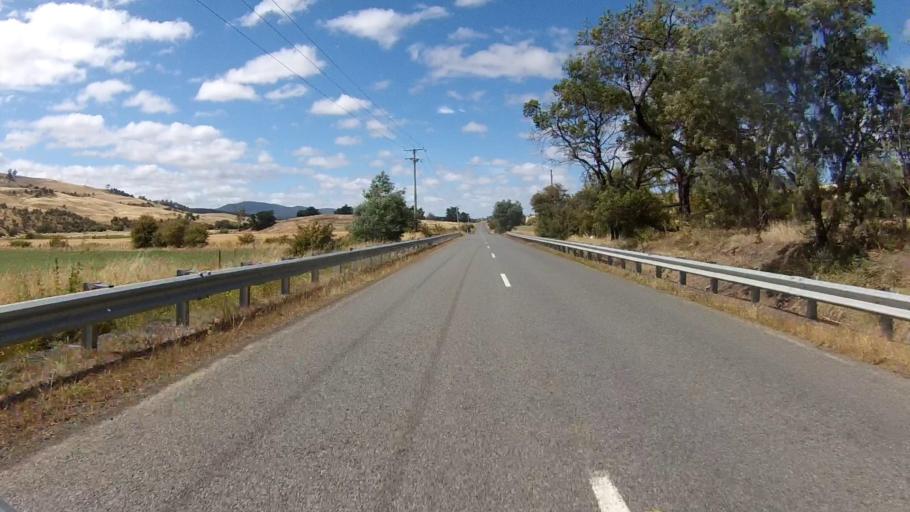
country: AU
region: Tasmania
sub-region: Brighton
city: Bridgewater
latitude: -42.5930
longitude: 147.4118
